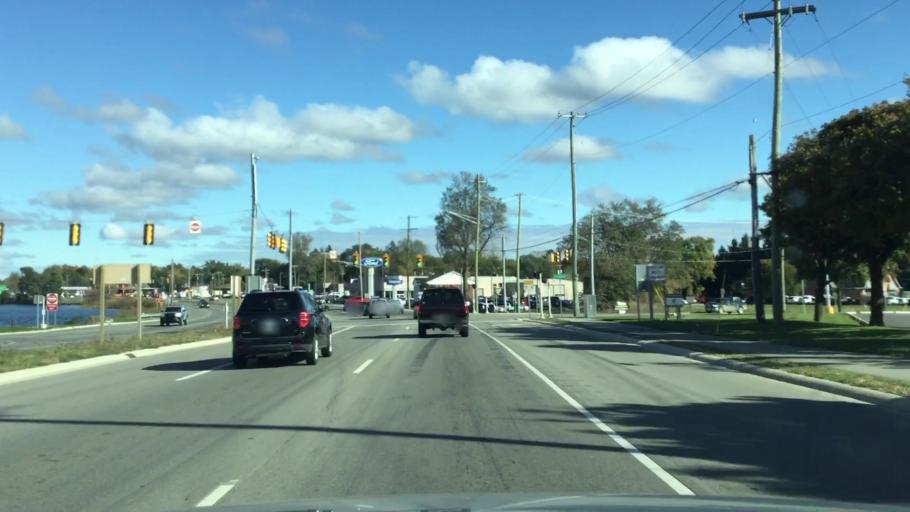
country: US
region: Michigan
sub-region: Oakland County
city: Lake Orion
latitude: 42.7670
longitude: -83.2396
